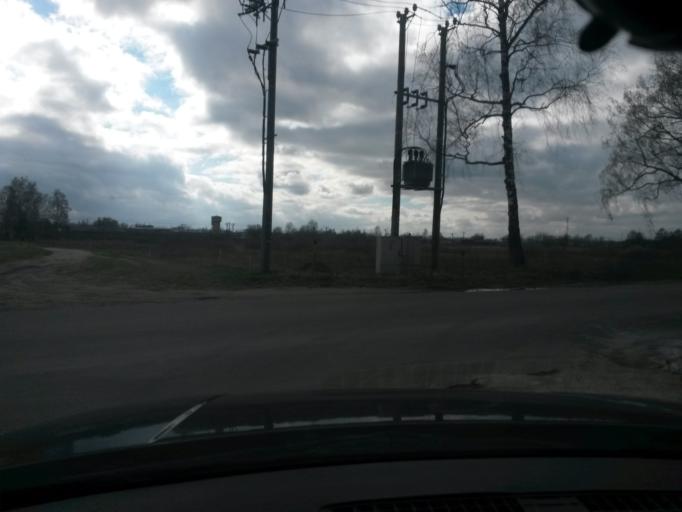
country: LV
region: Kekava
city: Kekava
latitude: 56.8921
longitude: 24.2427
